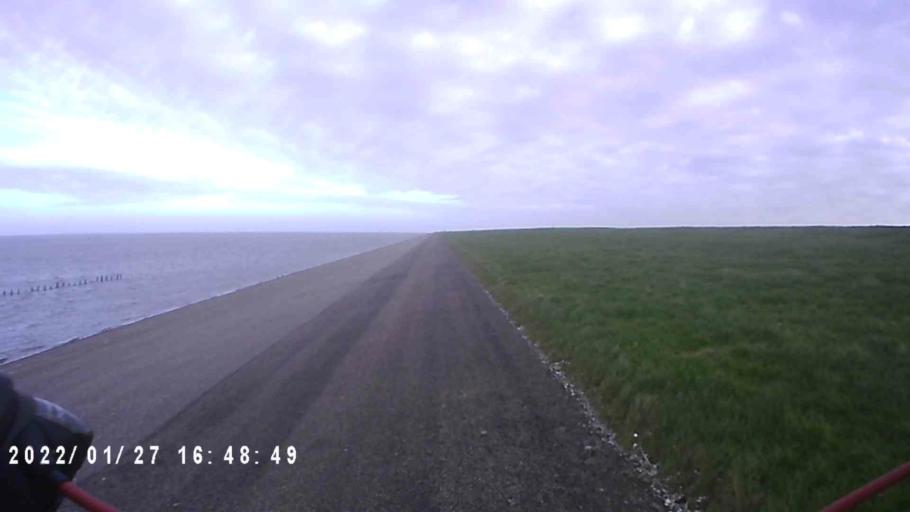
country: NL
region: Friesland
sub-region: Gemeente Dongeradeel
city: Ternaard
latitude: 53.4034
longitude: 6.0393
